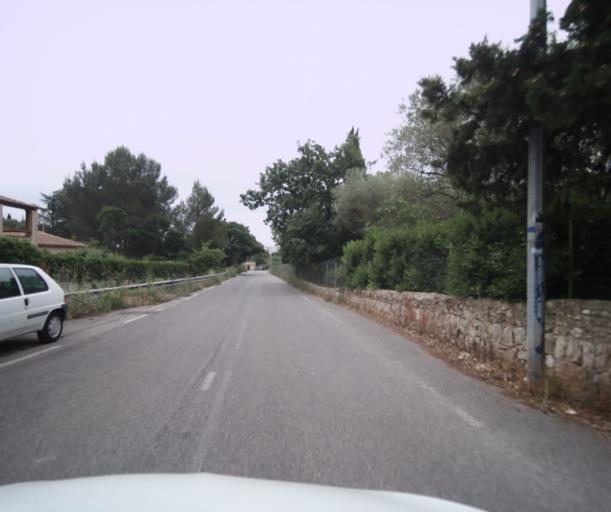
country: FR
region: Provence-Alpes-Cote d'Azur
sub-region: Departement du Var
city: Ollioules
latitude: 43.1447
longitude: 5.8832
